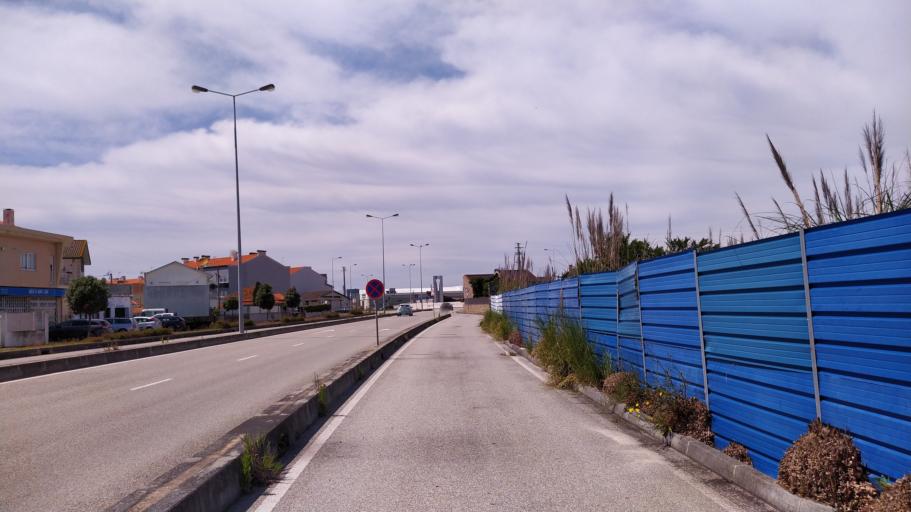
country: PT
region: Aveiro
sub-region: Ilhavo
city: Gafanha da Nazare
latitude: 40.6347
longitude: -8.6915
